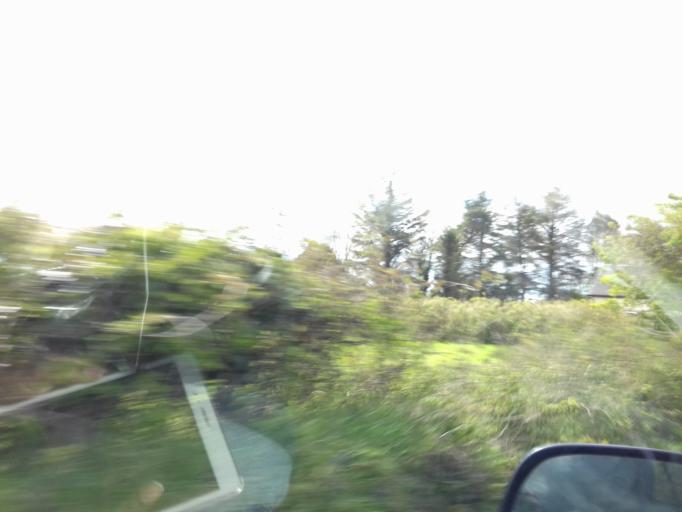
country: IE
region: Leinster
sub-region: Loch Garman
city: Loch Garman
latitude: 52.3013
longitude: -6.5615
